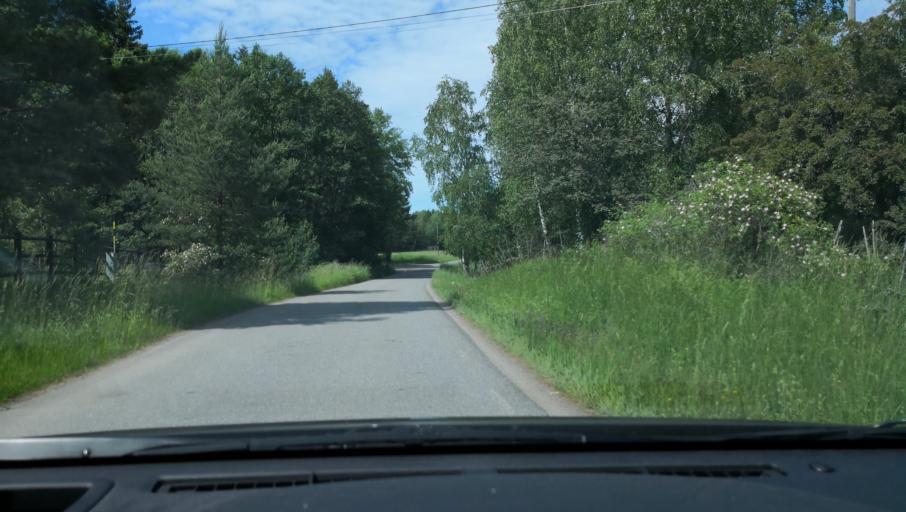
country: SE
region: Stockholm
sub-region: Sigtuna Kommun
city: Sigtuna
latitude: 59.6888
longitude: 17.6492
